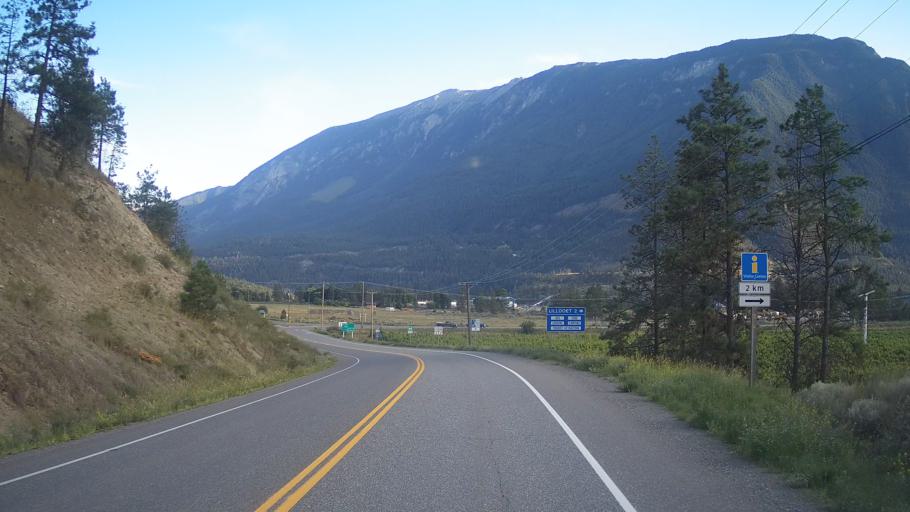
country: CA
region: British Columbia
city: Lillooet
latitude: 50.6880
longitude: -121.9194
